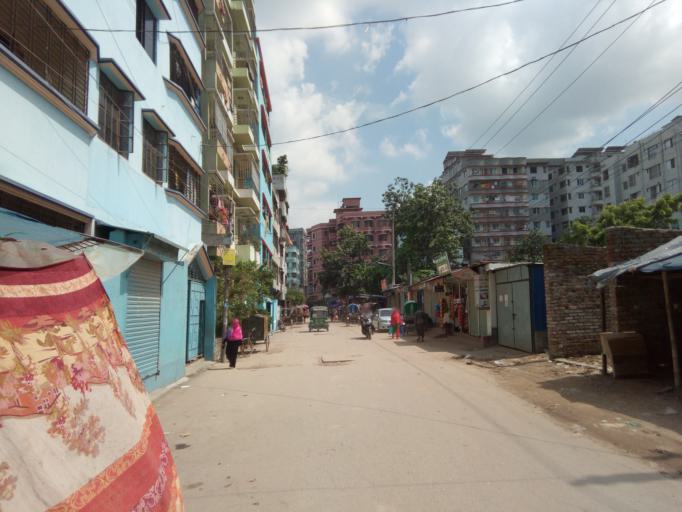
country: BD
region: Dhaka
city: Azimpur
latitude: 23.7422
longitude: 90.3634
